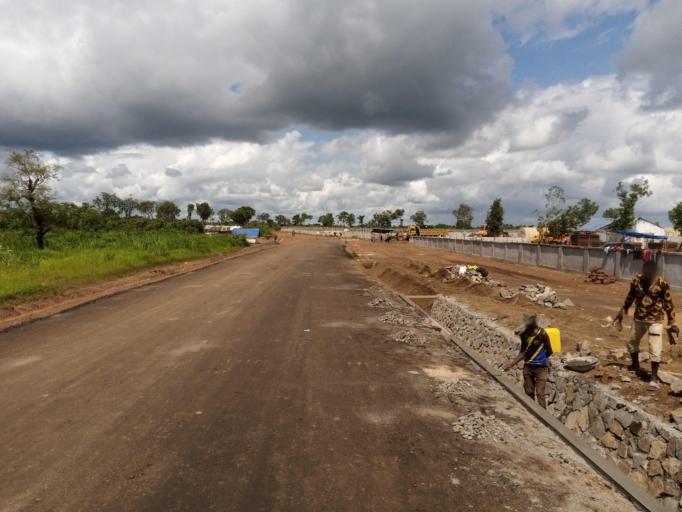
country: SL
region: Northern Province
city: Port Loko
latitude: 8.7761
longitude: -12.7618
